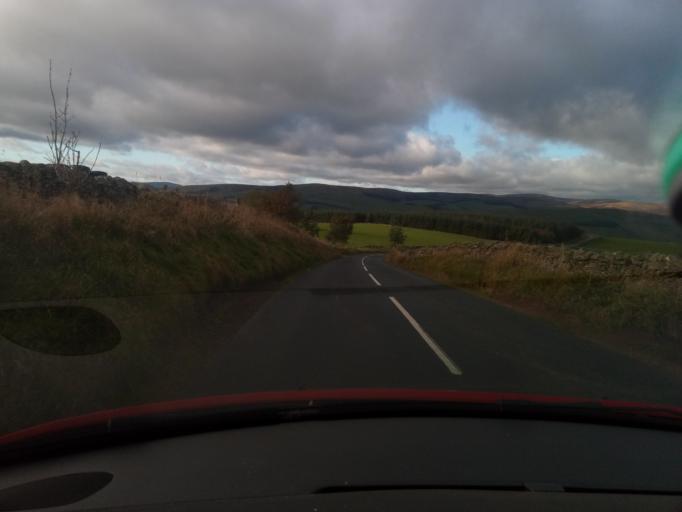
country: GB
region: Scotland
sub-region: The Scottish Borders
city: Galashiels
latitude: 55.6979
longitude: -2.8382
